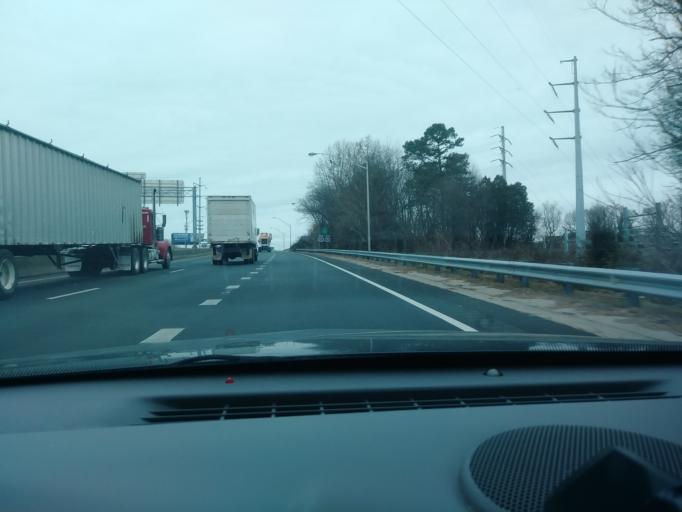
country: US
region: North Carolina
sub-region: Forsyth County
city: Winston-Salem
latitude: 36.0929
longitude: -80.2722
